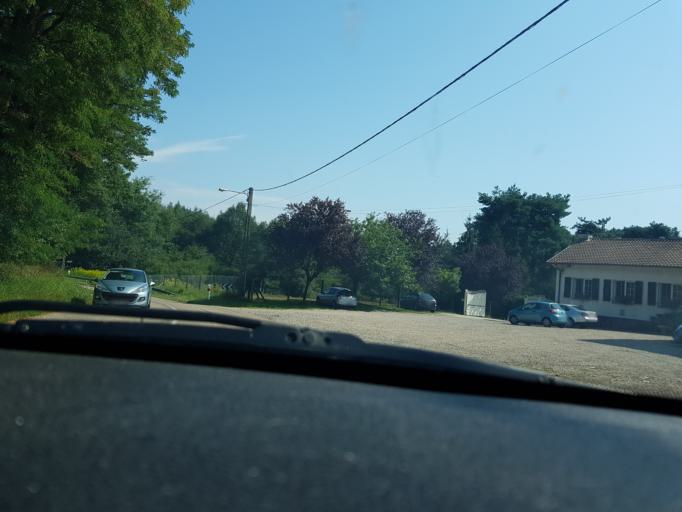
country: FR
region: Lorraine
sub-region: Departement de la Moselle
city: Porcelette
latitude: 49.1347
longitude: 6.6692
